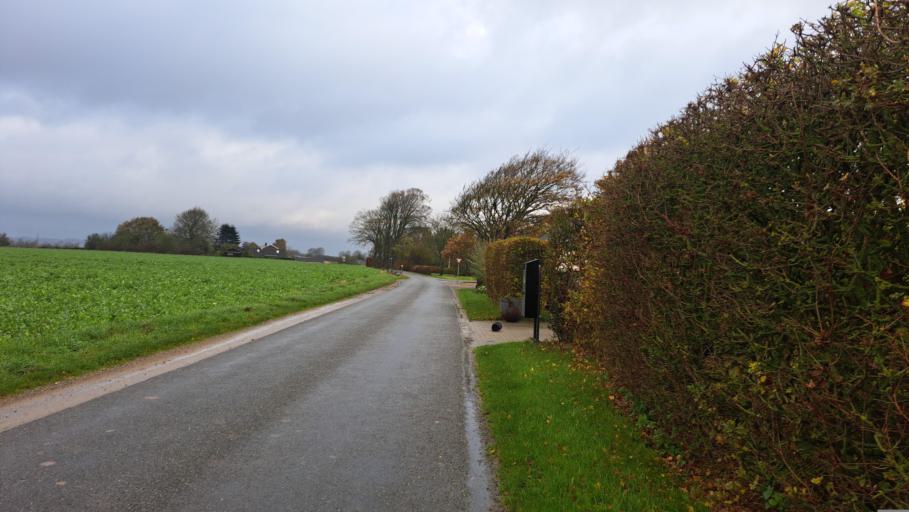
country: DK
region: Central Jutland
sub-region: Hedensted Kommune
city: Hedensted
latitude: 55.8348
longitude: 9.7361
